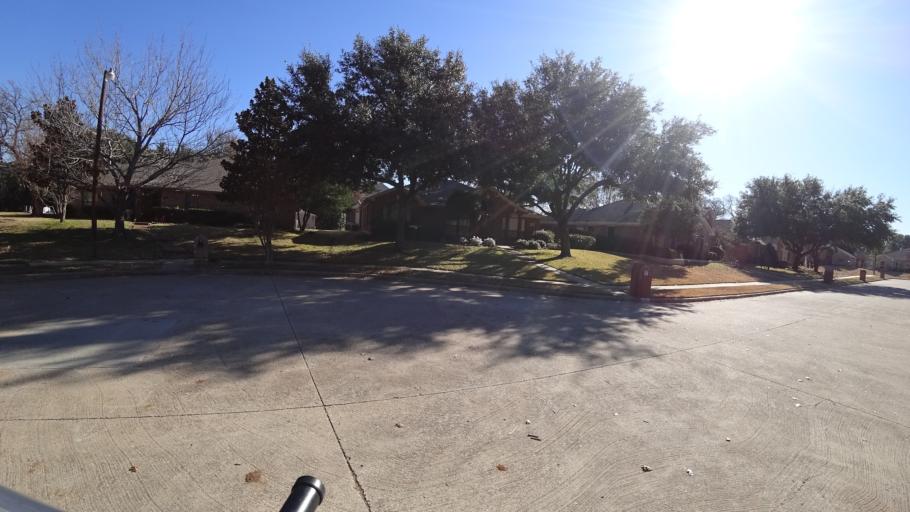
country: US
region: Texas
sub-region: Denton County
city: Lewisville
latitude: 33.0200
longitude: -97.0254
